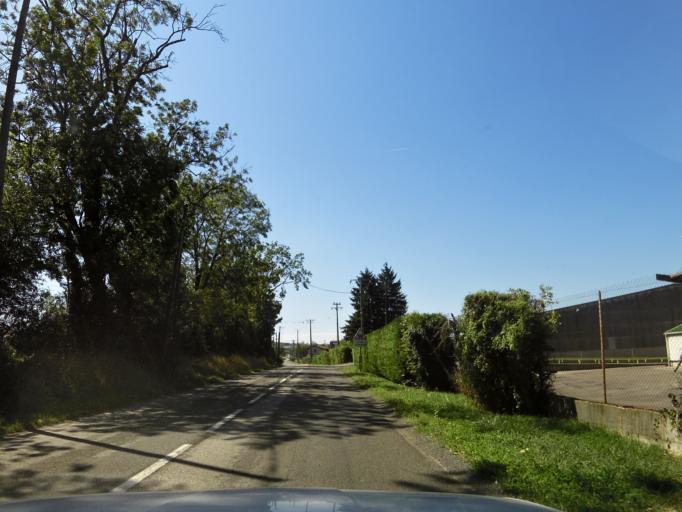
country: FR
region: Rhone-Alpes
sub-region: Departement de l'Ain
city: Vaux-en-Bugey
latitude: 45.9270
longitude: 5.3446
